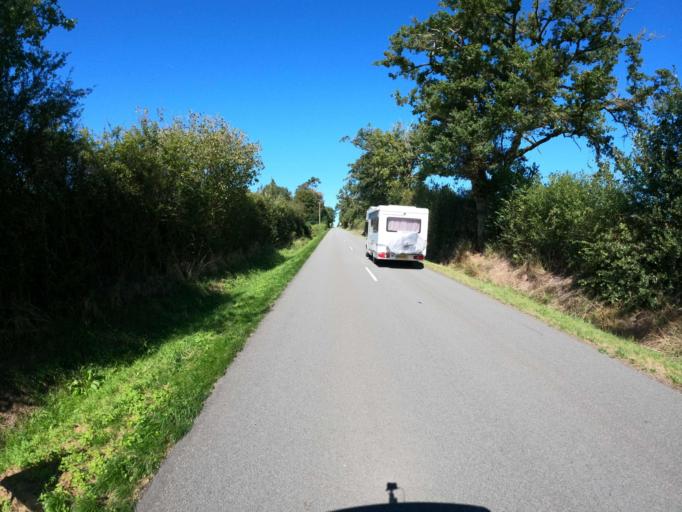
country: FR
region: Limousin
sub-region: Departement de la Haute-Vienne
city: Le Dorat
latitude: 46.2368
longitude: 1.0570
